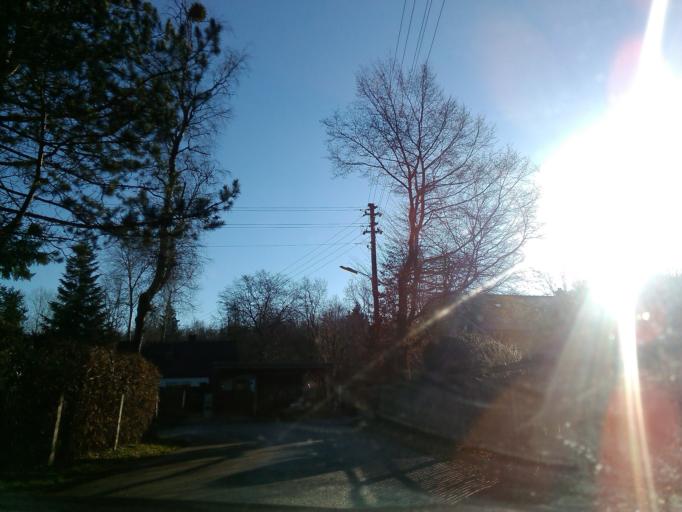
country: DE
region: Bavaria
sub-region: Upper Bavaria
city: Gauting
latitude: 48.0516
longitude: 11.3610
